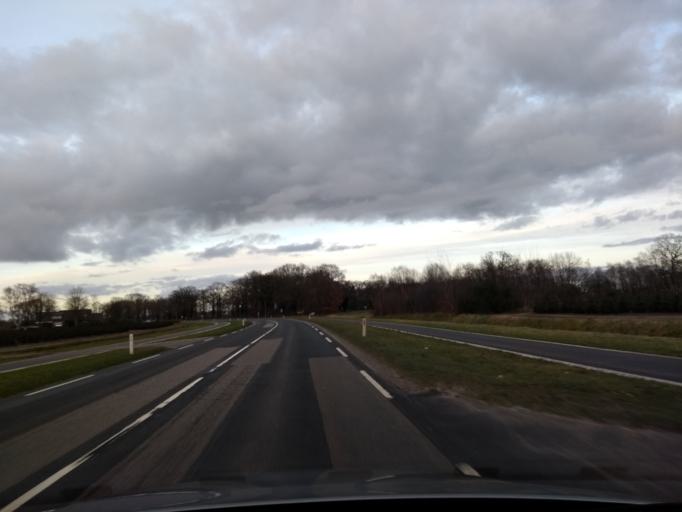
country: NL
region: Overijssel
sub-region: Gemeente Oldenzaal
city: Oldenzaal
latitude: 52.3091
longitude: 6.8599
